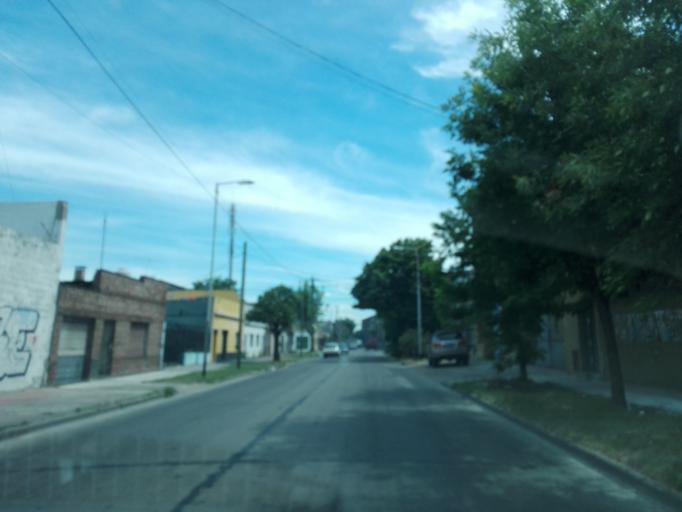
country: AR
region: Buenos Aires
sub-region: Partido de Avellaneda
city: Avellaneda
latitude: -34.6916
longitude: -58.3549
